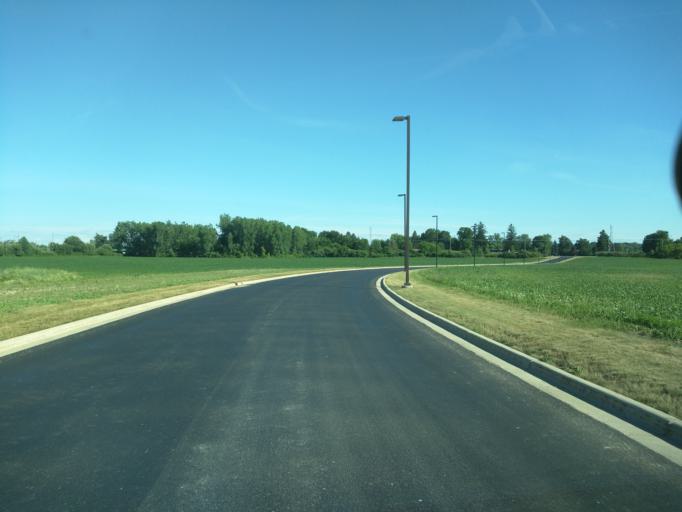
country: US
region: Michigan
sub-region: Eaton County
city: Waverly
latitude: 42.7159
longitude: -84.6364
